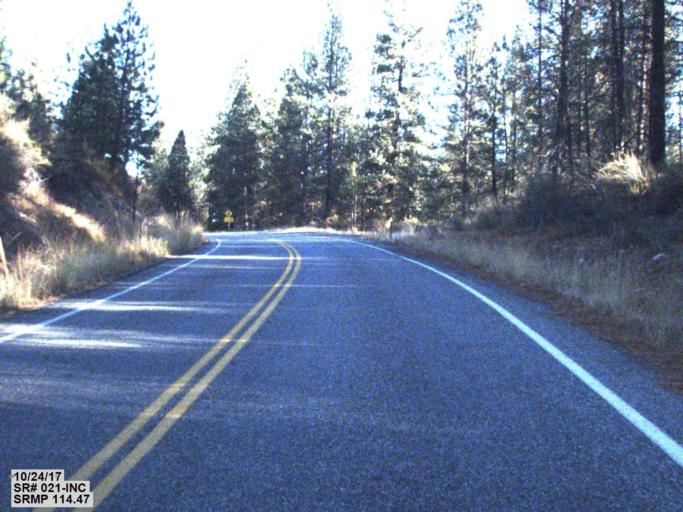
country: US
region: Washington
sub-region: Okanogan County
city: Coulee Dam
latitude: 48.0492
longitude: -118.6689
